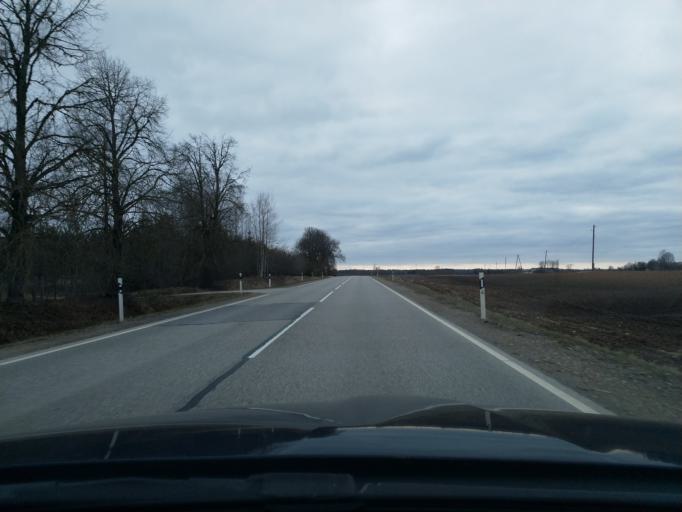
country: LV
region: Kuldigas Rajons
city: Kuldiga
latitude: 56.9631
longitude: 22.0699
